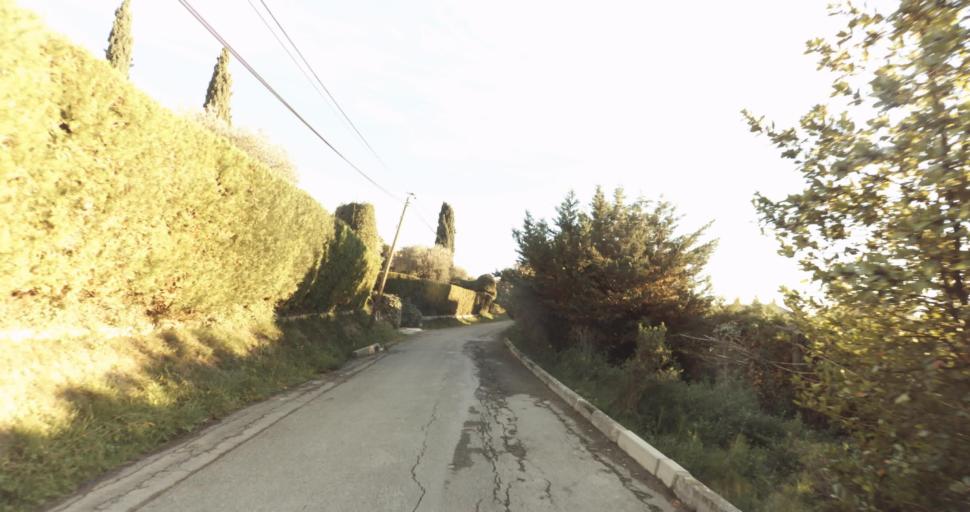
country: FR
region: Provence-Alpes-Cote d'Azur
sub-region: Departement des Alpes-Maritimes
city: Vence
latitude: 43.7302
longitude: 7.0898
